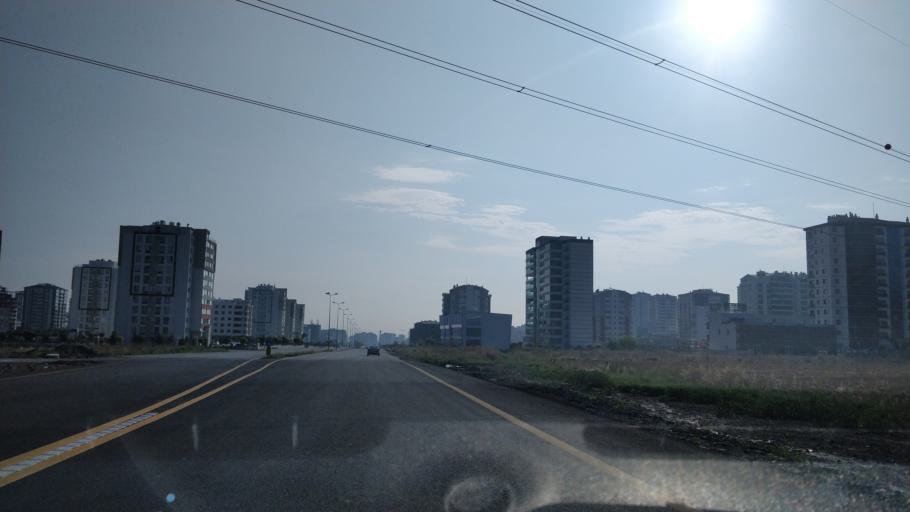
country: TR
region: Ankara
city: Etimesgut
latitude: 39.8863
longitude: 32.6139
